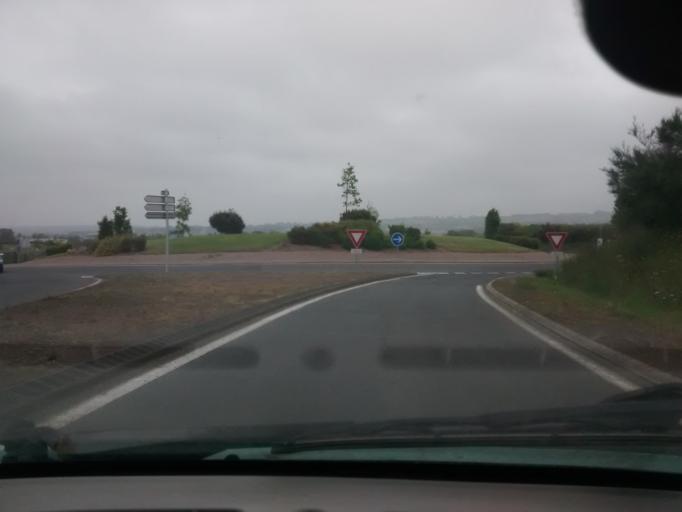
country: FR
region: Lower Normandy
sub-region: Departement de la Manche
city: Torigni-sur-Vire
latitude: 49.0484
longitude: -1.0016
